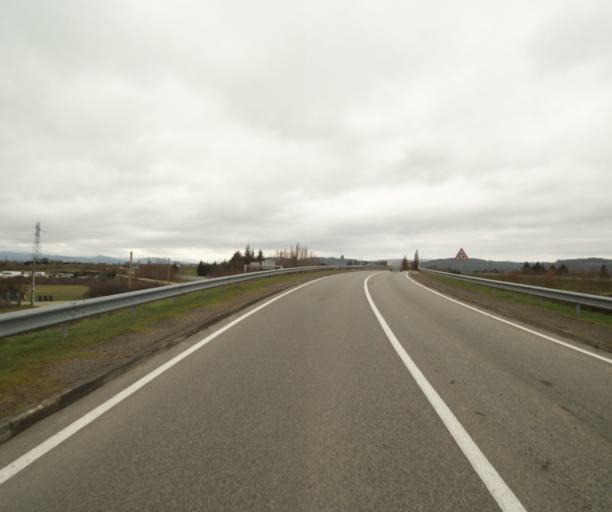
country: FR
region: Midi-Pyrenees
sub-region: Departement de l'Ariege
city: Pamiers
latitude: 43.1365
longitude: 1.6263
